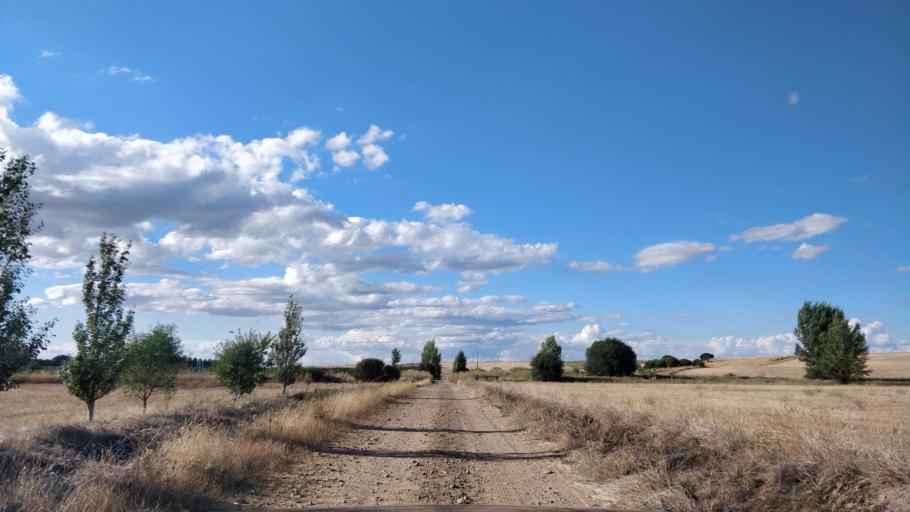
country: ES
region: Castille and Leon
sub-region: Provincia de Leon
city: Valverde-Enrique
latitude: 42.3297
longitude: -5.2798
